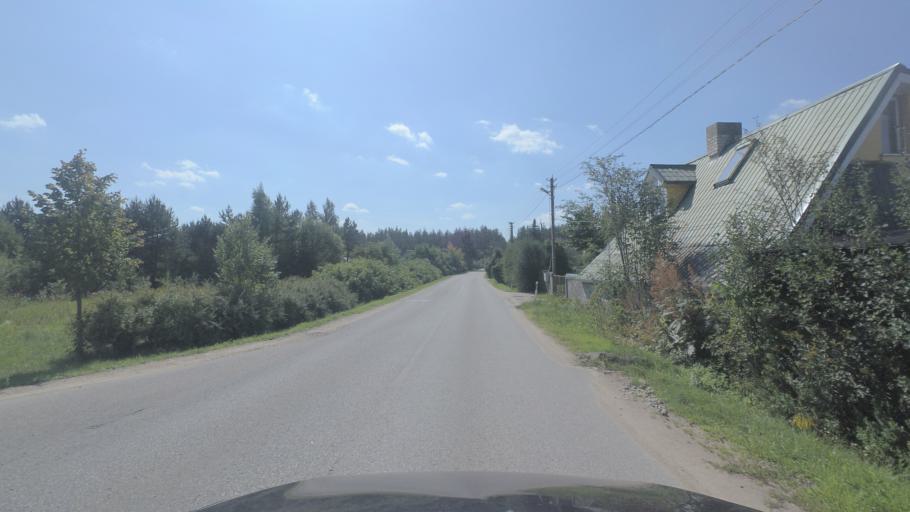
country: LT
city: Nemencine
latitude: 54.8286
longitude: 25.3636
